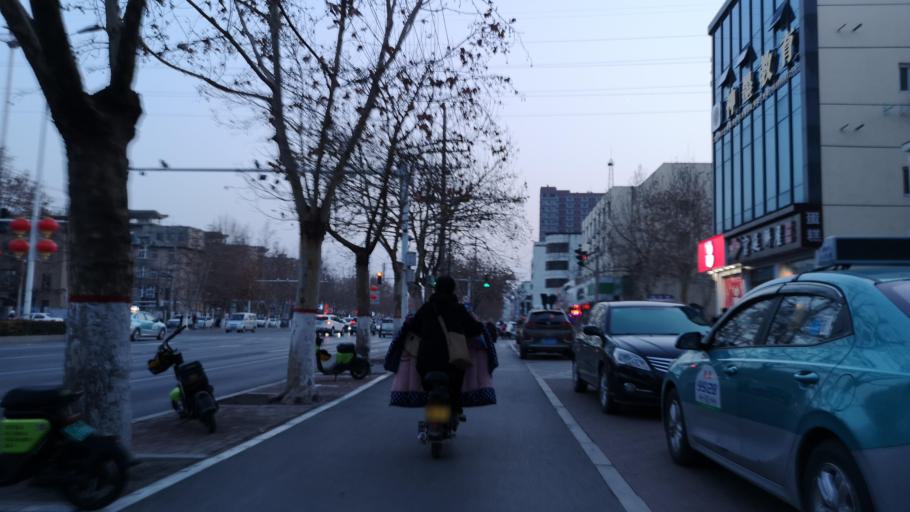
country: CN
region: Henan Sheng
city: Zhongyuanlu
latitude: 35.7662
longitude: 115.0683
